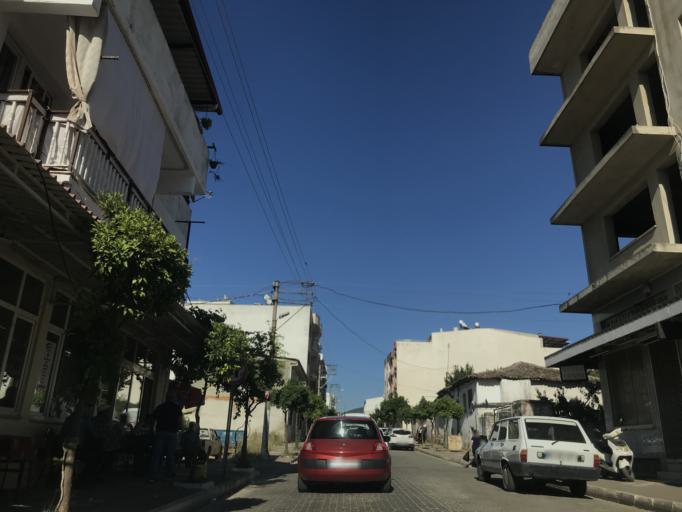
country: TR
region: Aydin
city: Davutlar
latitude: 37.7328
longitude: 27.2883
